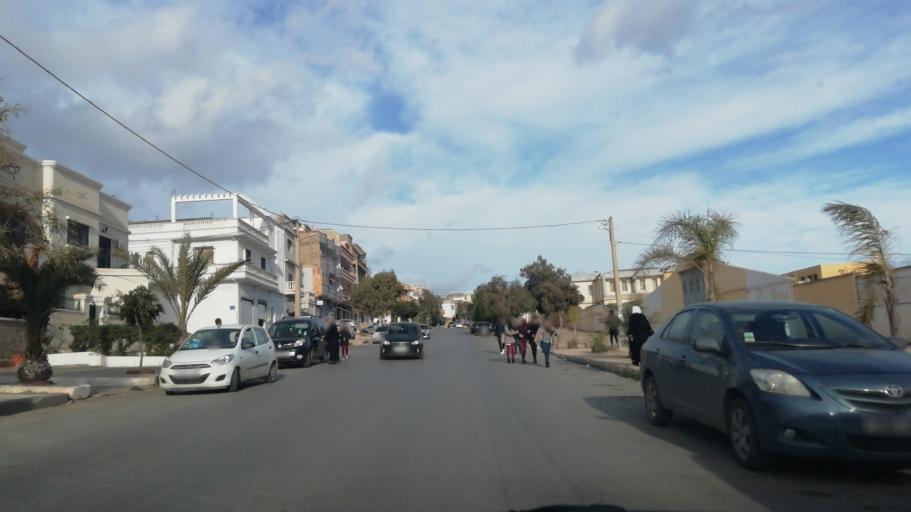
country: DZ
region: Oran
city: Bir el Djir
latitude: 35.7286
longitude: -0.5718
